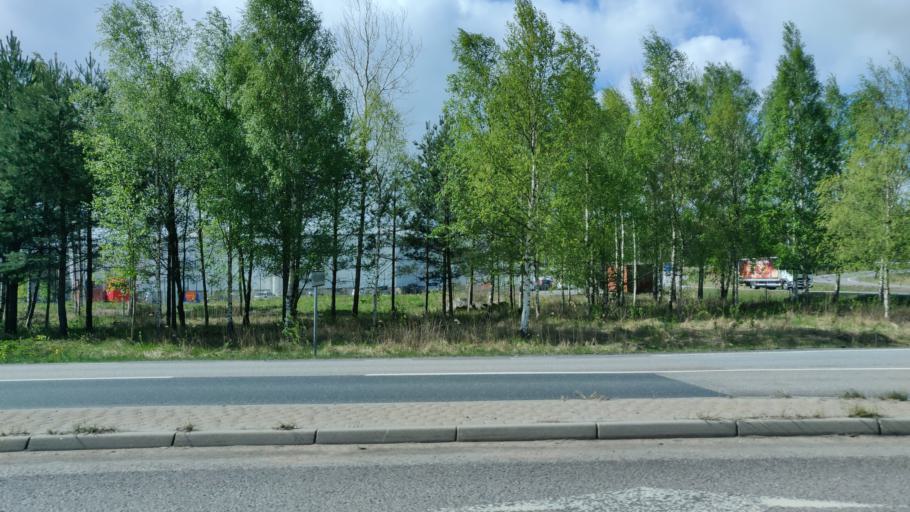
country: SE
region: Vaermland
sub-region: Karlstads Kommun
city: Skattkarr
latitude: 59.3964
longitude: 13.5830
